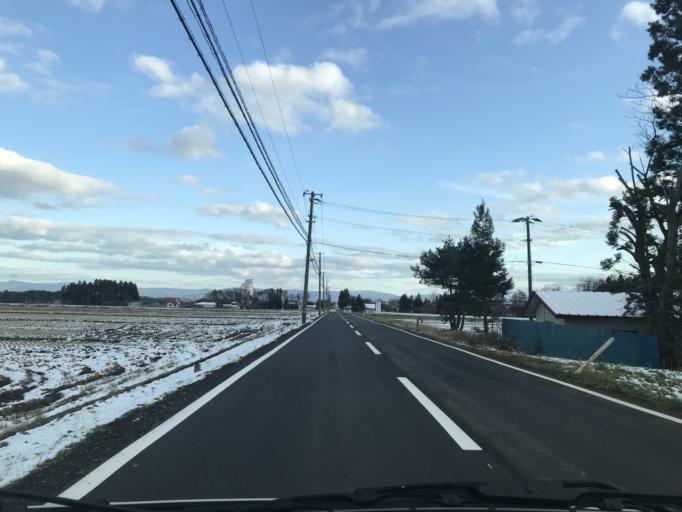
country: JP
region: Iwate
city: Kitakami
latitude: 39.2075
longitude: 141.0422
